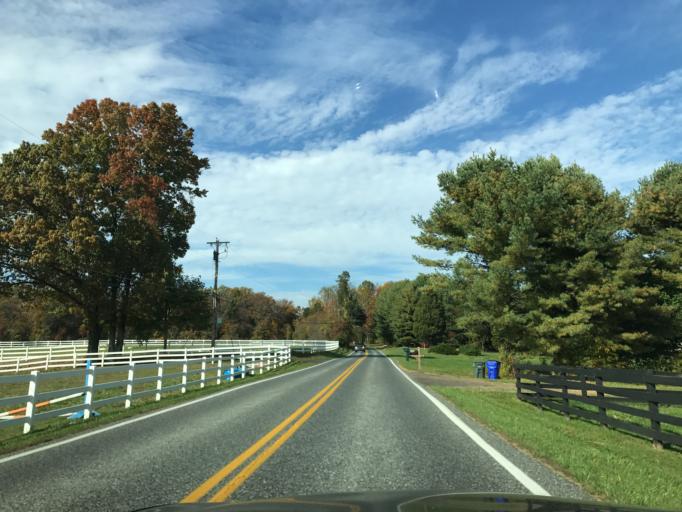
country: US
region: Maryland
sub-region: Harford County
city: Joppatowne
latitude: 39.4564
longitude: -76.3753
